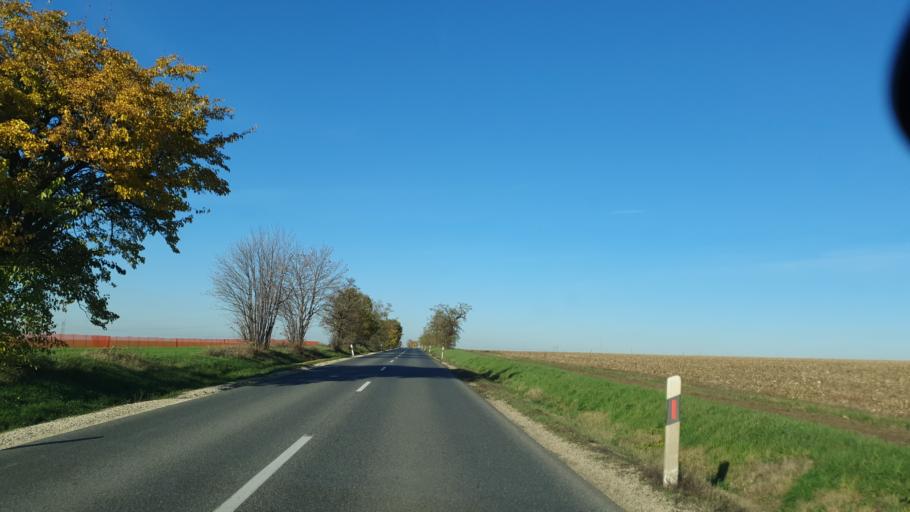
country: HU
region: Fejer
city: Zamoly
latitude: 47.2689
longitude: 18.4199
